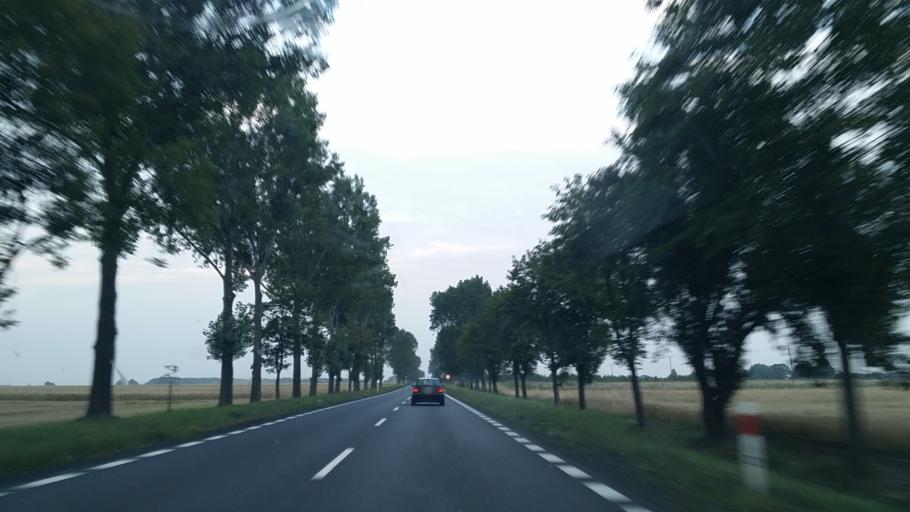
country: PL
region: Lower Silesian Voivodeship
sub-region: Powiat legnicki
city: Prochowice
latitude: 51.3278
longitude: 16.3097
